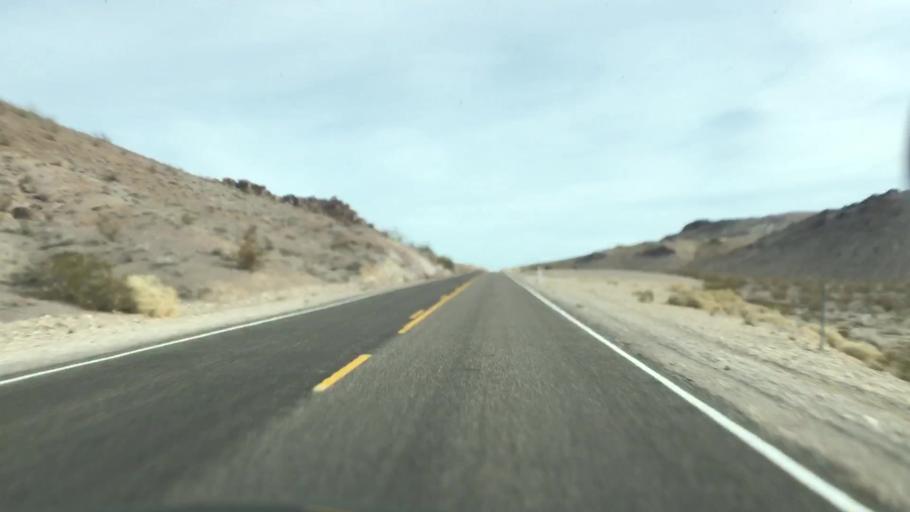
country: US
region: Nevada
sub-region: Nye County
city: Beatty
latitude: 36.8937
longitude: -116.8015
